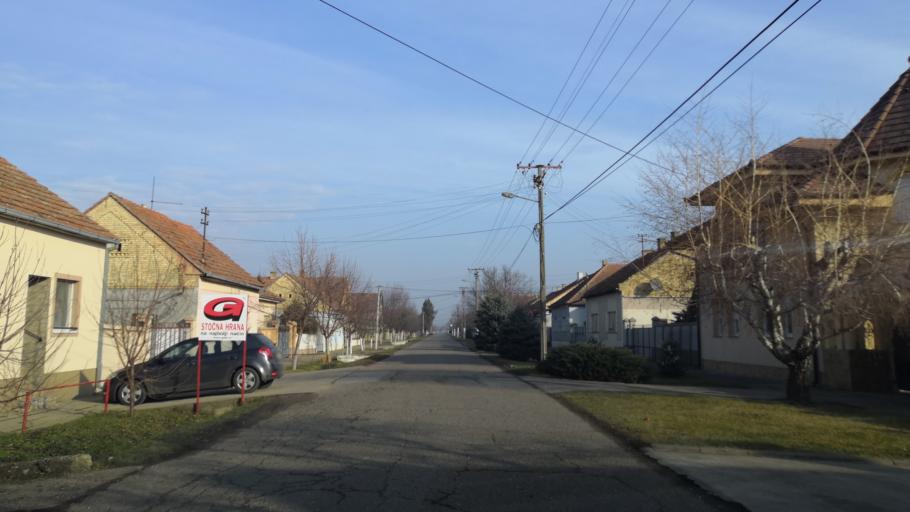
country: RS
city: Kisac
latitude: 45.3482
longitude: 19.7329
